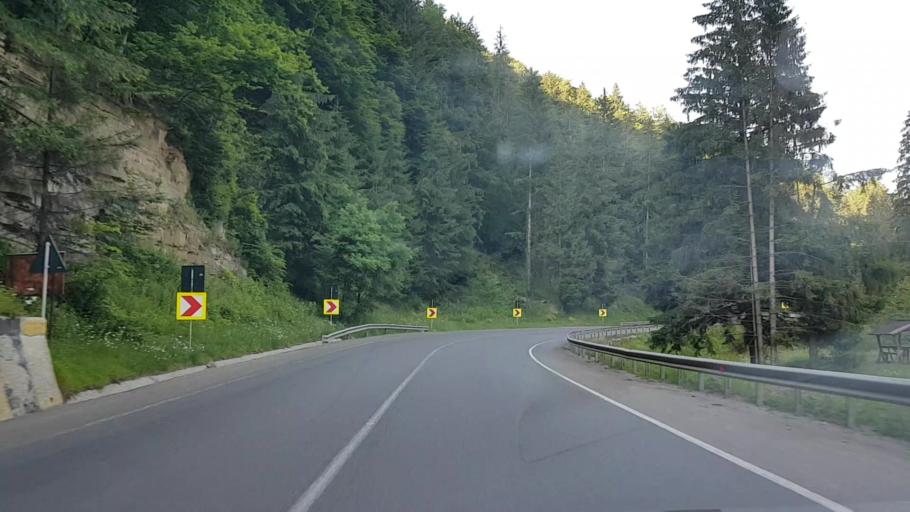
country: RO
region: Bistrita-Nasaud
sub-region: Comuna Tiha Bargaului
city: Tureac
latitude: 47.2186
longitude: 24.8968
